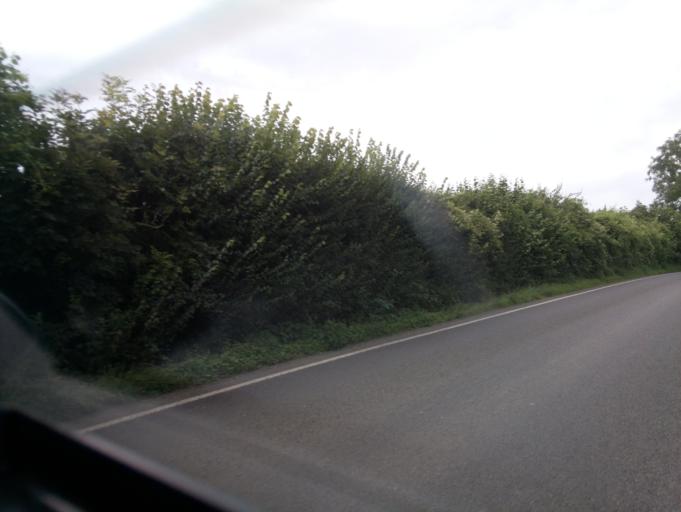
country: GB
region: England
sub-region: Somerset
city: Street
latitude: 51.0854
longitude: -2.6943
